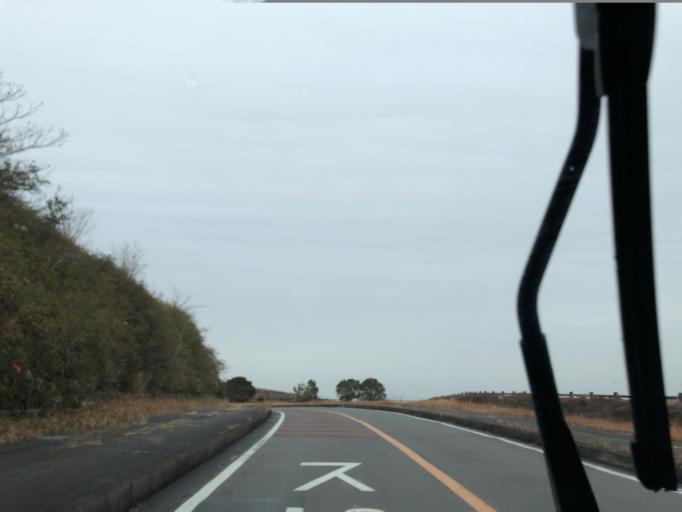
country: JP
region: Wakayama
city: Tanabe
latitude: 33.6660
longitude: 135.3586
